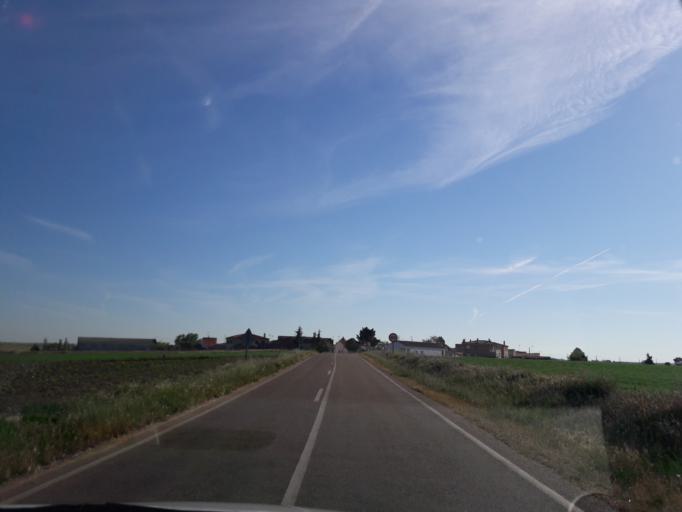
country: ES
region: Castille and Leon
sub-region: Provincia de Salamanca
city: Palencia de Negrilla
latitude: 41.0710
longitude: -5.6186
